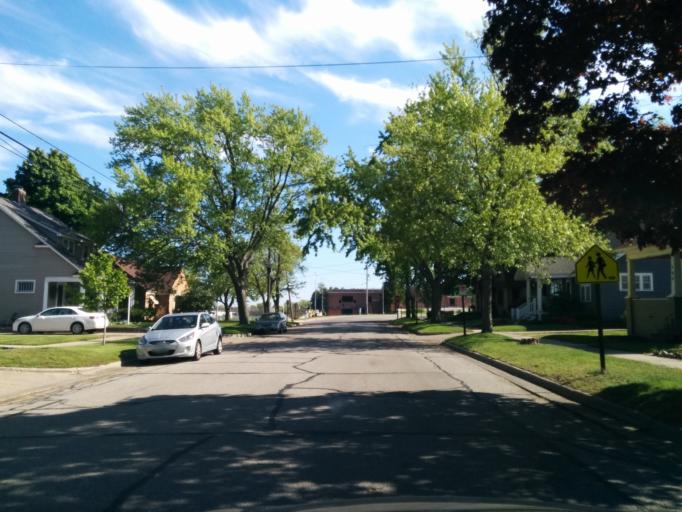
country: US
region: Michigan
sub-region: Ottawa County
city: Grand Haven
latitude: 43.0578
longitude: -86.2246
